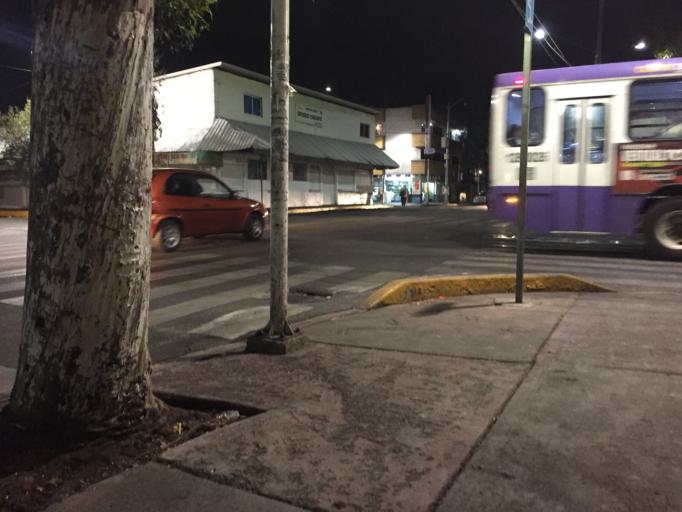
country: MX
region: Mexico City
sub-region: Iztacalco
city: Iztacalco
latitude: 19.3929
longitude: -99.0634
